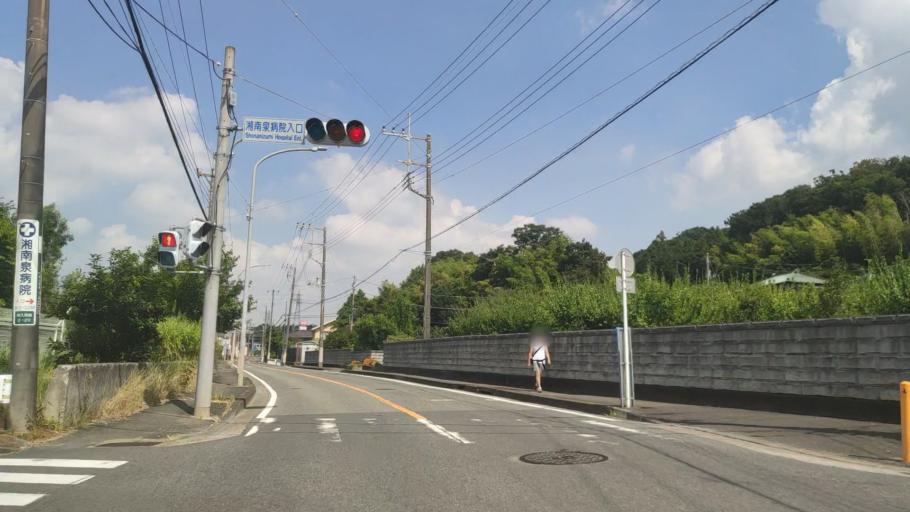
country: JP
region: Kanagawa
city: Minami-rinkan
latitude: 35.4428
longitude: 139.5072
